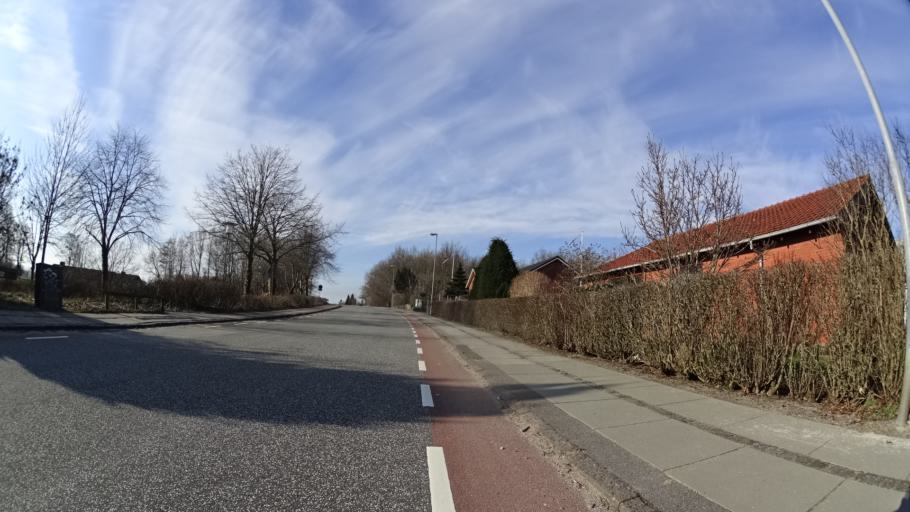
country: DK
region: Central Jutland
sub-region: Arhus Kommune
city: Kolt
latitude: 56.1078
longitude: 10.0920
